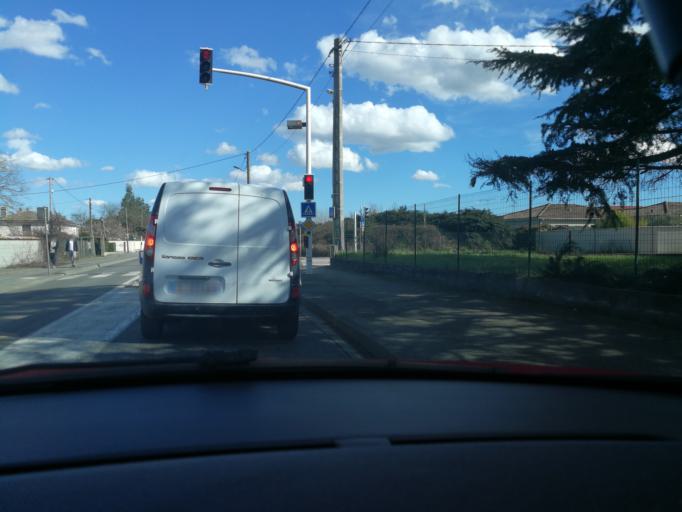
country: FR
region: Midi-Pyrenees
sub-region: Departement de la Haute-Garonne
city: Cugnaux
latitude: 43.5607
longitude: 1.3514
